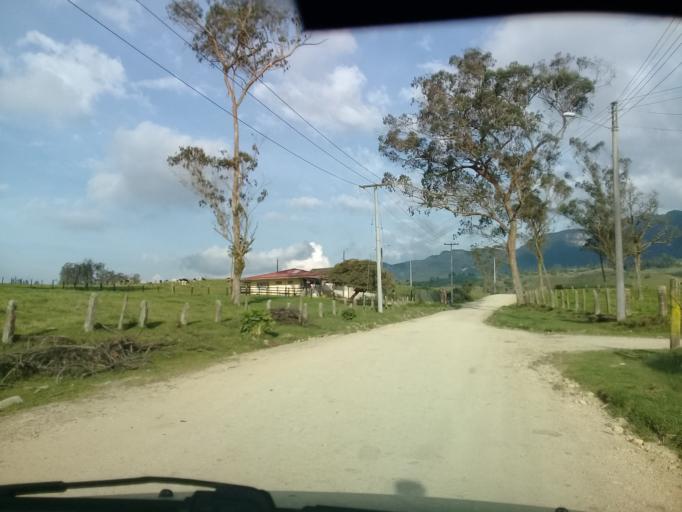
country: CO
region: Cundinamarca
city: Sibate
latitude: 4.4270
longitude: -74.2897
